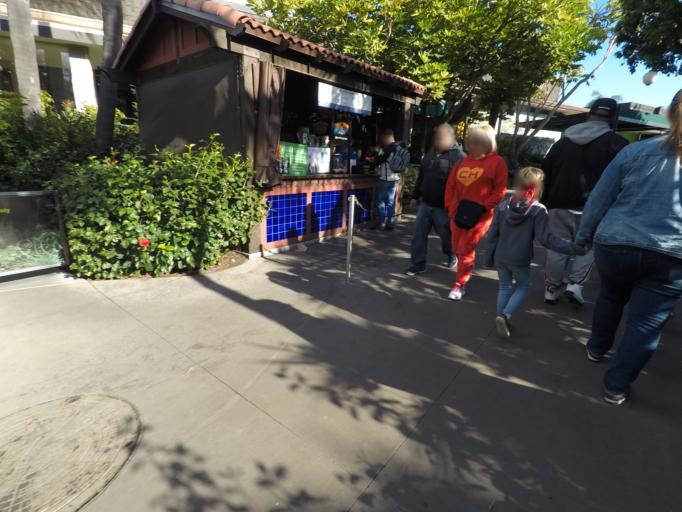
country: US
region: California
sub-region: San Diego County
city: San Diego
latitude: 32.7354
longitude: -117.1496
